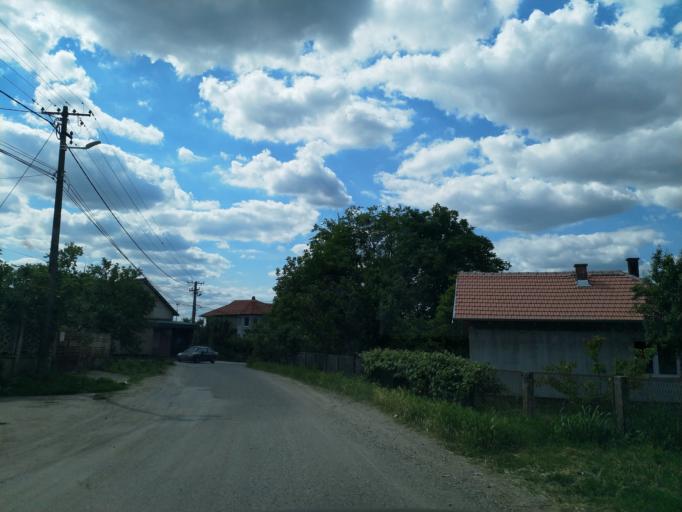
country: RS
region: Central Serbia
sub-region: Pomoravski Okrug
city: Jagodina
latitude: 43.9424
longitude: 21.2996
